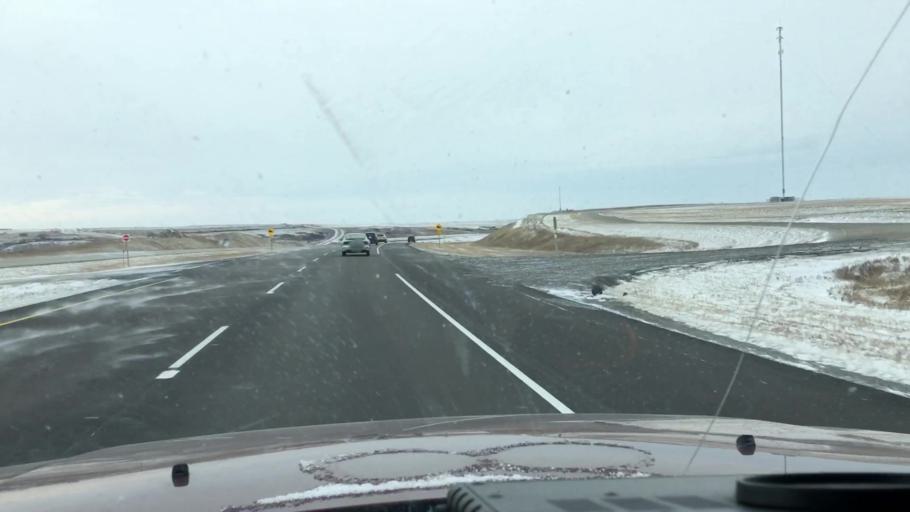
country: CA
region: Saskatchewan
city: Saskatoon
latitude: 51.7401
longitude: -106.4764
